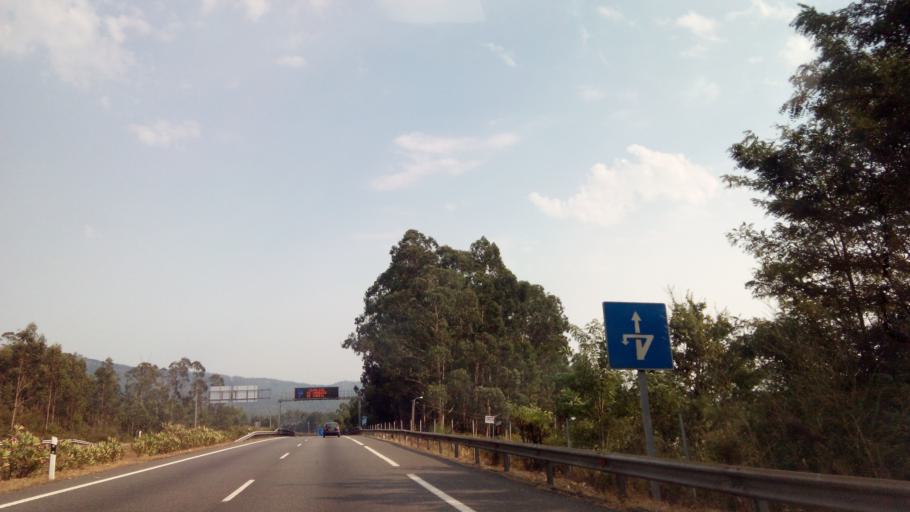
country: ES
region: Galicia
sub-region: Provincia de Pontevedra
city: Porrino
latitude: 42.1661
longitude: -8.6143
